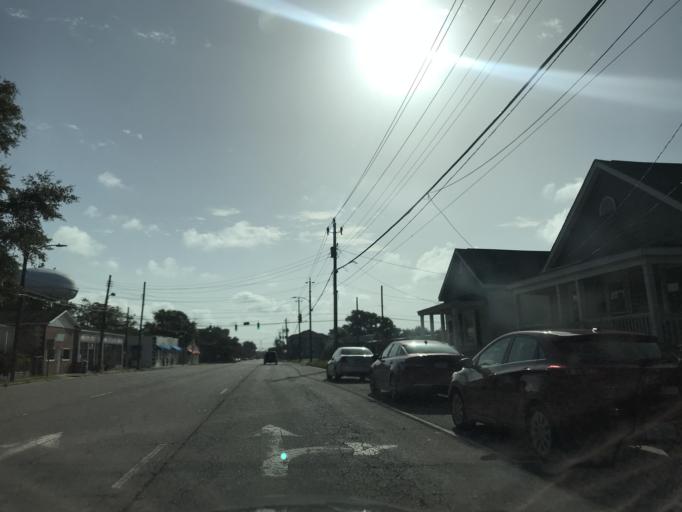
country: US
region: North Carolina
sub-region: New Hanover County
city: Wilmington
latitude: 34.2246
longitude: -77.9389
